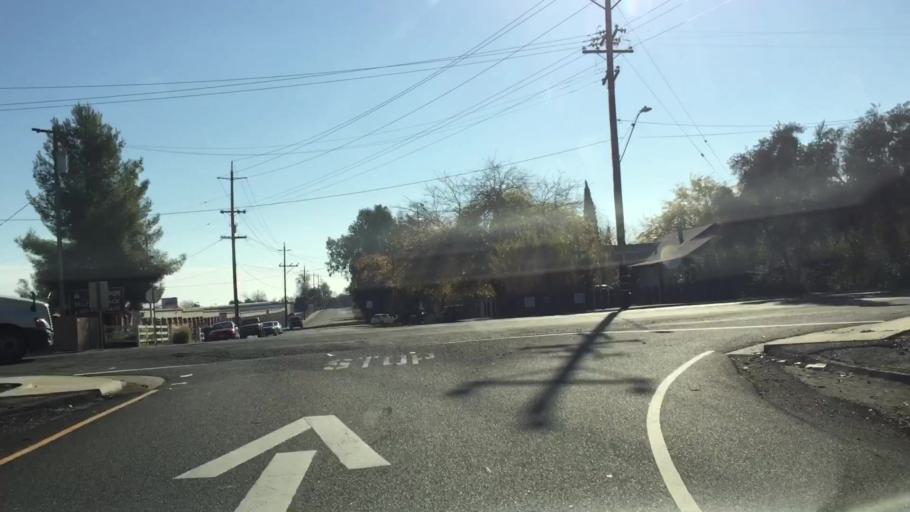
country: US
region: California
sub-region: Butte County
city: Thermalito
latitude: 39.5243
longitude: -121.5739
